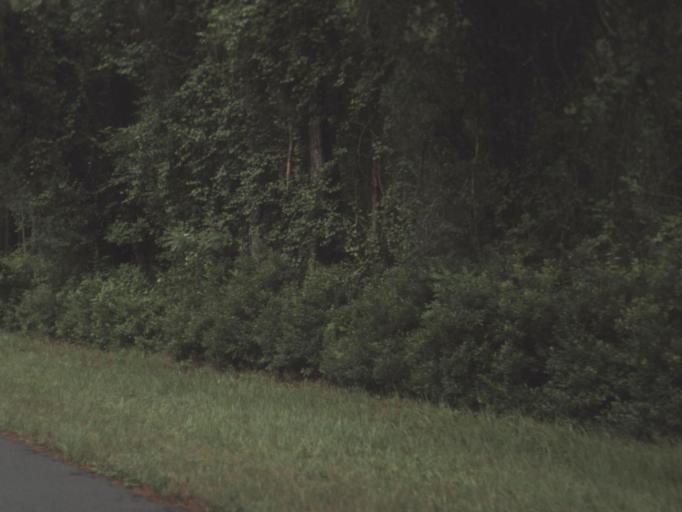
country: US
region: Florida
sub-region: Hamilton County
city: Jasper
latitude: 30.5705
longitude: -82.6799
